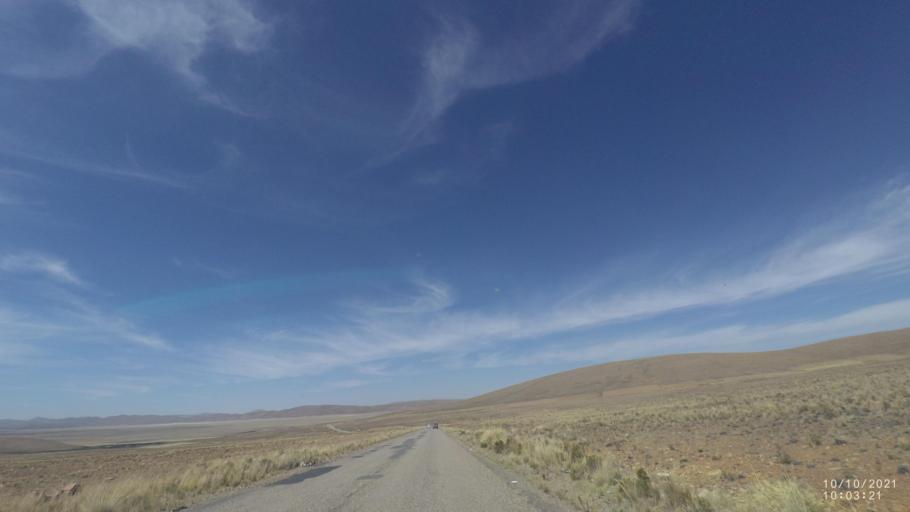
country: BO
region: La Paz
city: Eucaliptus
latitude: -17.3682
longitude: -67.4397
